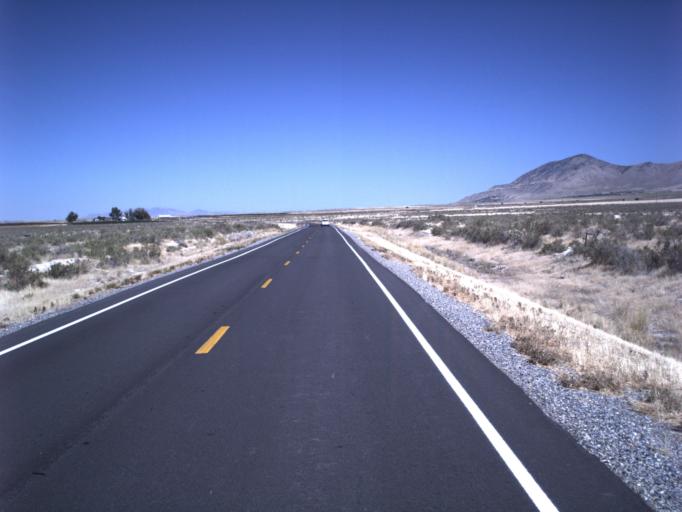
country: US
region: Utah
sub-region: Tooele County
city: Grantsville
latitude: 40.4791
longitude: -112.7456
